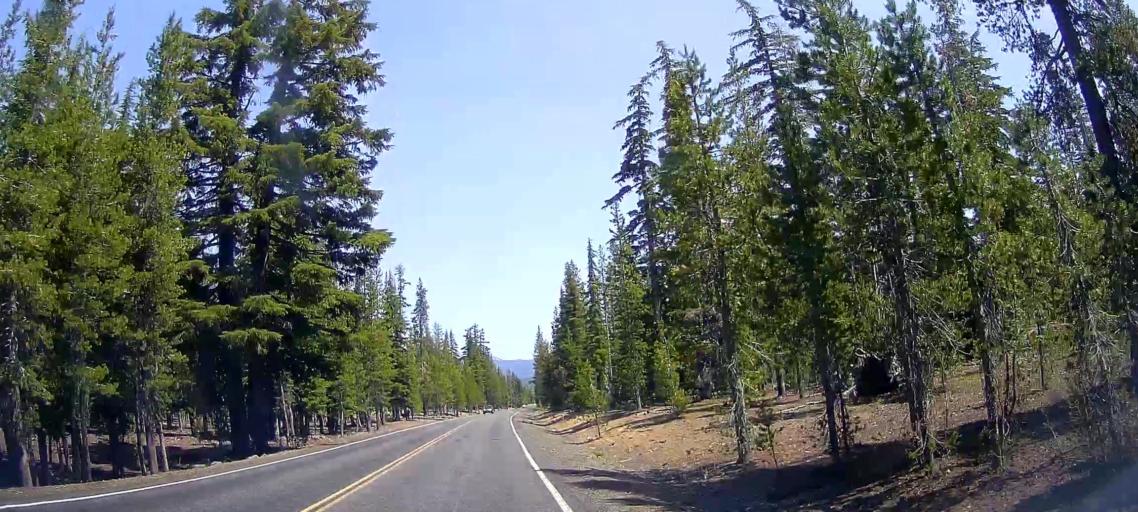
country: US
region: Oregon
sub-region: Jackson County
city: Shady Cove
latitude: 43.0069
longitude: -122.1327
